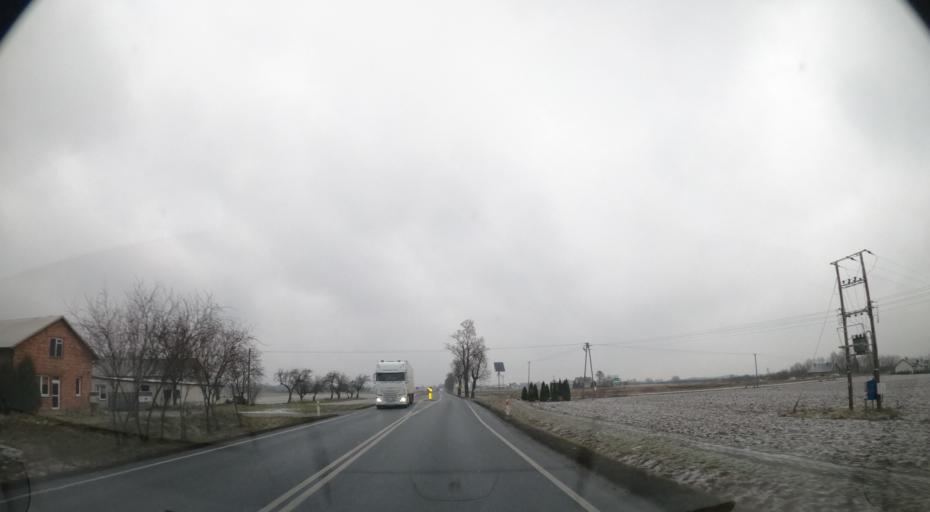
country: PL
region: Masovian Voivodeship
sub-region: Powiat sochaczewski
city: Mlodzieszyn
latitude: 52.2743
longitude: 20.1696
